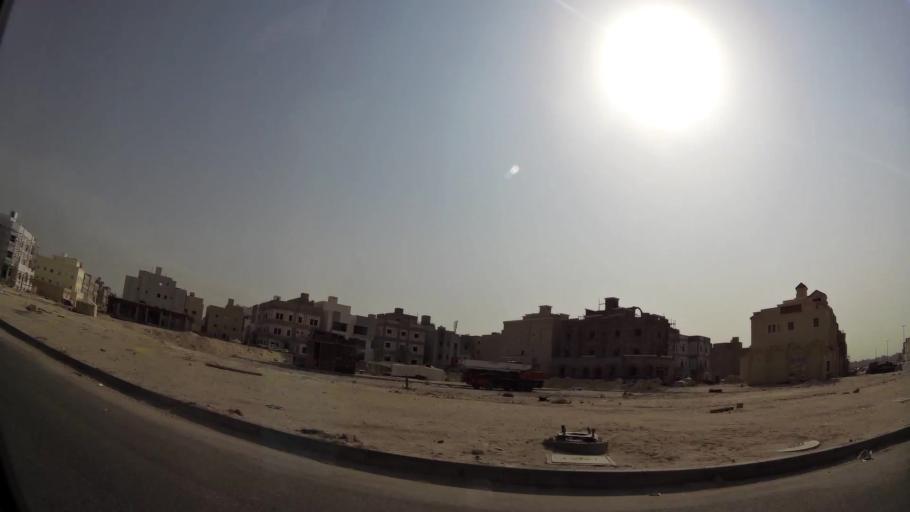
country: KW
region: Muhafazat al Jahra'
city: Al Jahra'
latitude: 29.3509
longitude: 47.7716
